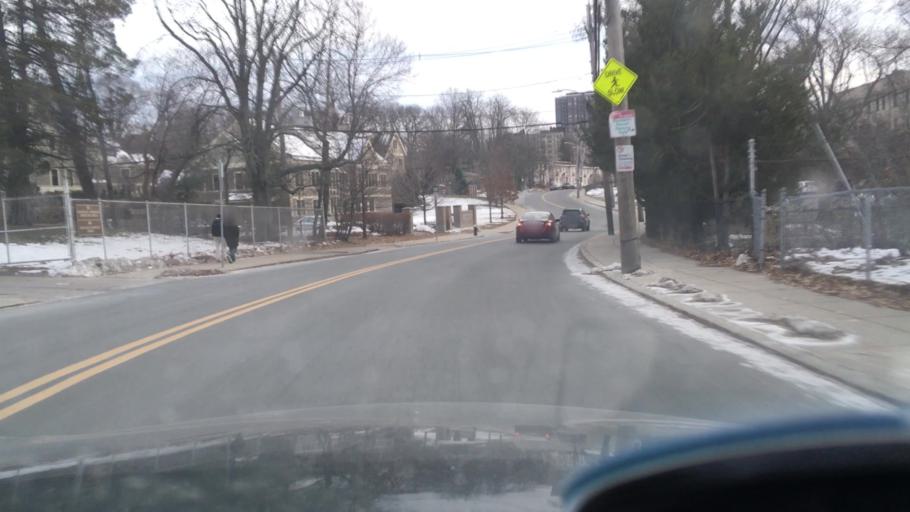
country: US
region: Massachusetts
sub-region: Middlesex County
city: Watertown
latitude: 42.3450
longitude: -71.1577
